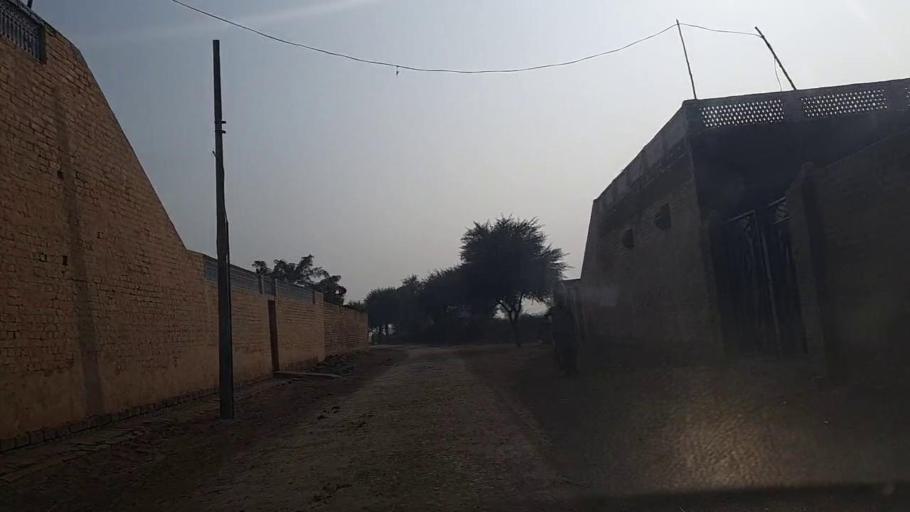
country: PK
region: Sindh
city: Sanghar
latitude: 26.0788
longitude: 68.8755
